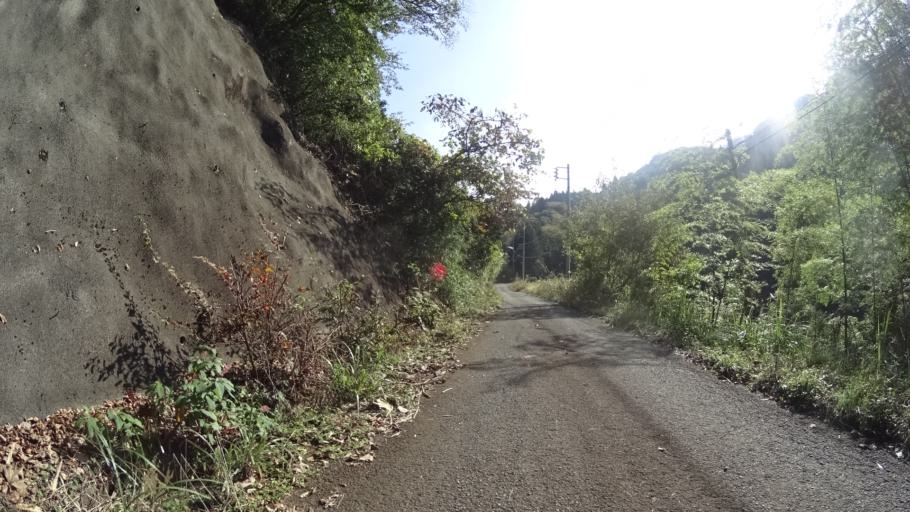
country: JP
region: Yamanashi
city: Otsuki
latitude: 35.5821
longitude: 138.9732
